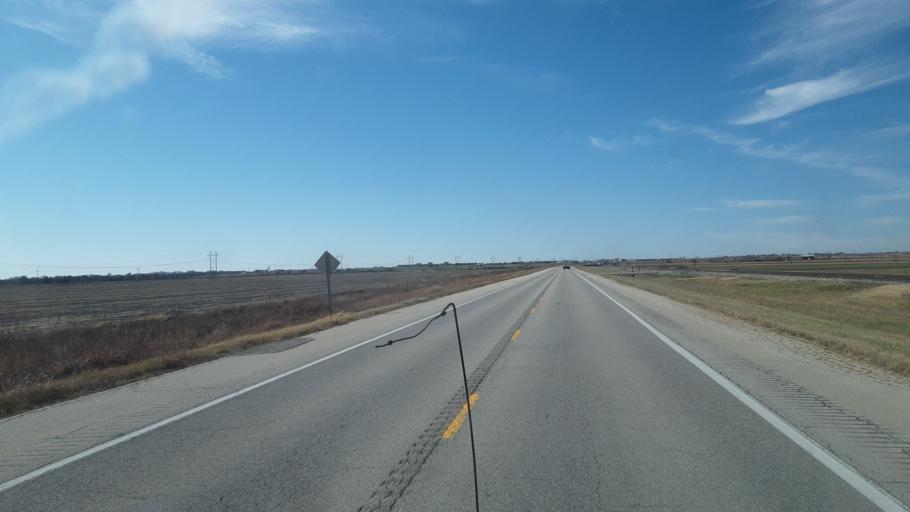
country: US
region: Kansas
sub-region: McPherson County
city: McPherson
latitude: 38.3658
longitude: -97.7424
